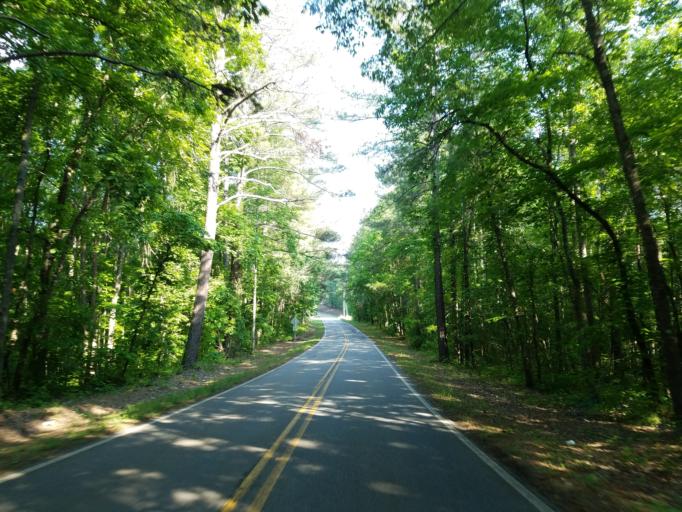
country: US
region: Georgia
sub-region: Pickens County
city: Nelson
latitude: 34.3748
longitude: -84.3380
